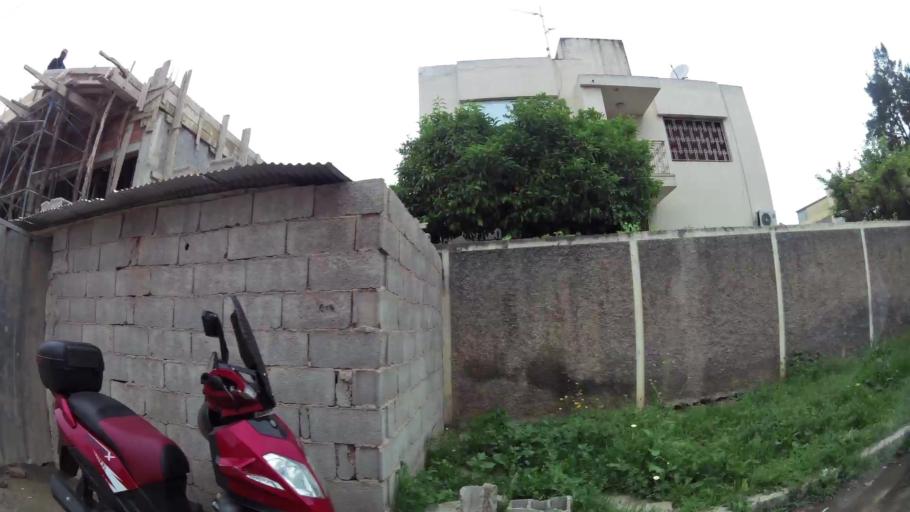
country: MA
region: Fes-Boulemane
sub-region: Fes
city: Fes
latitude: 34.0327
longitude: -5.0119
